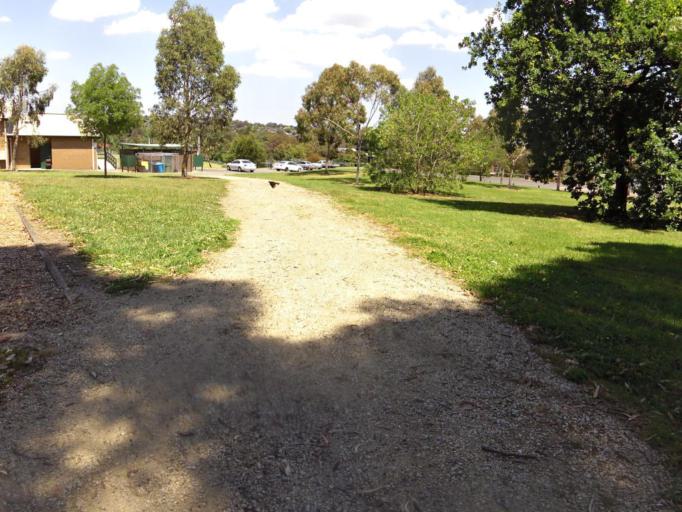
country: AU
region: Victoria
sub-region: Casey
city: Endeavour Hills
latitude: -37.9851
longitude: 145.2514
